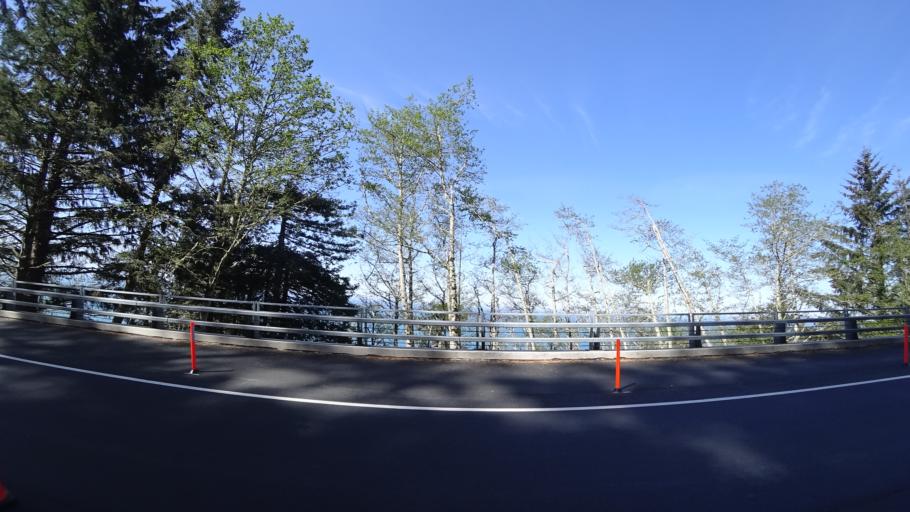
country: US
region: California
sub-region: Del Norte County
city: Bertsch-Oceanview
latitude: 41.6341
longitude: -124.1154
